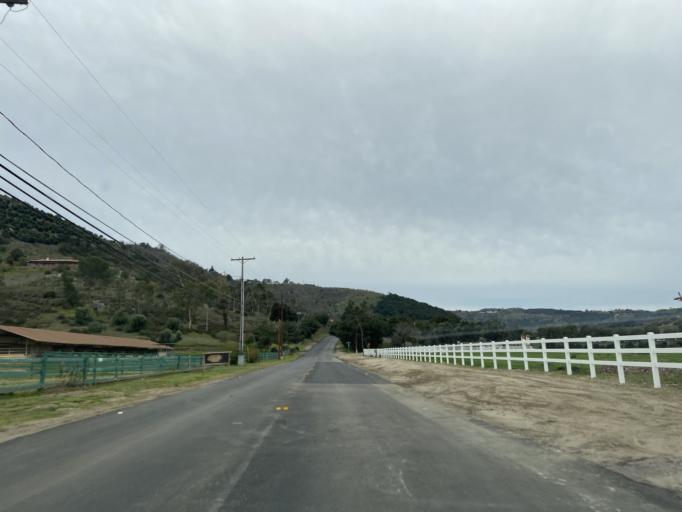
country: US
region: California
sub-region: San Diego County
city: Valley Center
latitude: 33.3104
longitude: -117.0093
